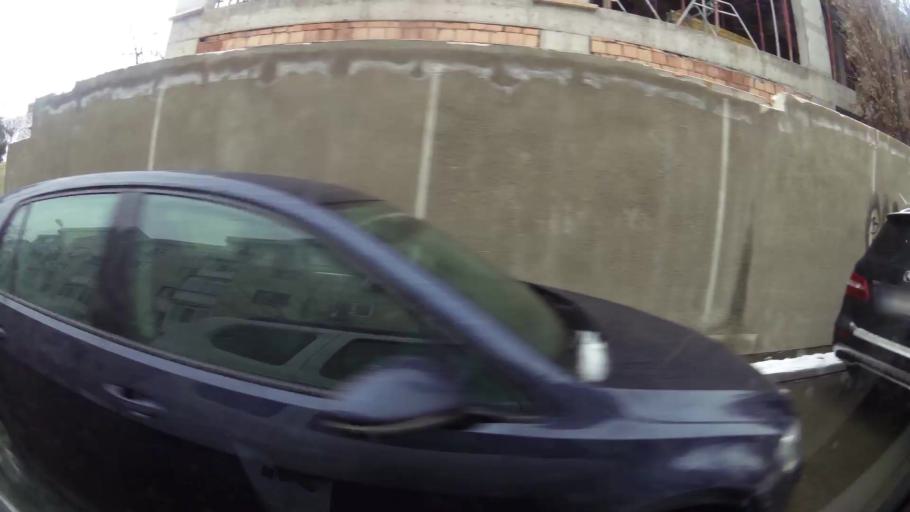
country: RO
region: Prahova
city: Ploiesti
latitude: 44.9387
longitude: 26.0023
